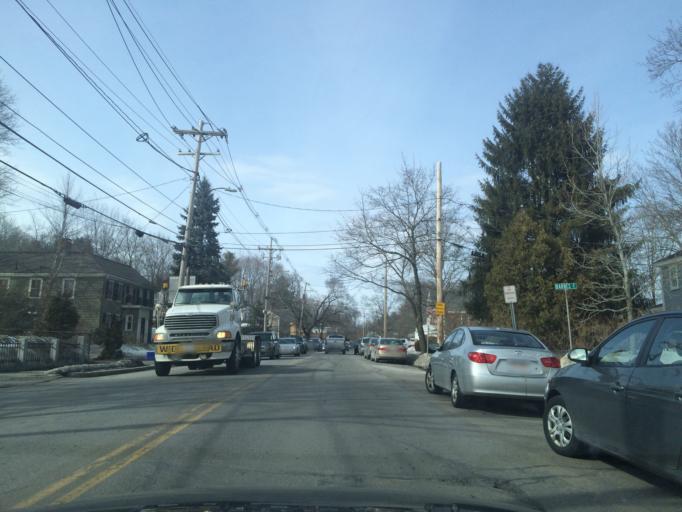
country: US
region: Massachusetts
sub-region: Middlesex County
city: Lexington
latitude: 42.4296
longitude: -71.2073
